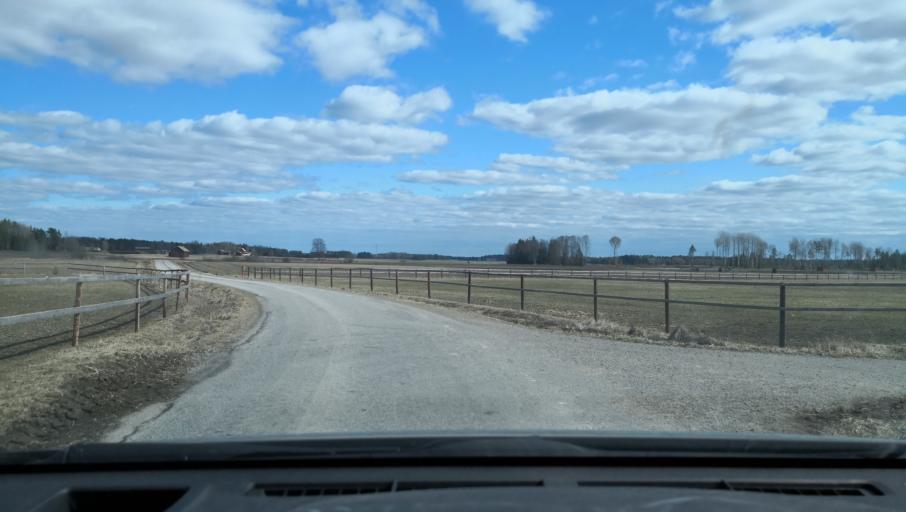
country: SE
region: Vaestmanland
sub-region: Sala Kommun
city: Sala
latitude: 59.8617
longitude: 16.5766
